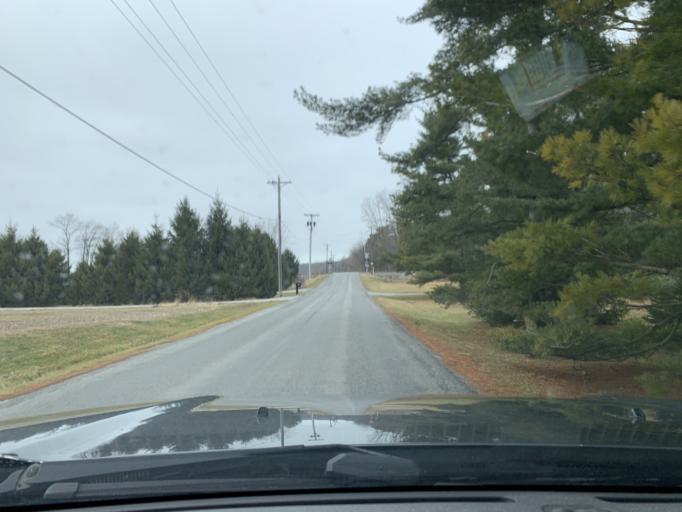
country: US
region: Indiana
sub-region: Porter County
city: Chesterton
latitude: 41.6022
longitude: -86.9899
